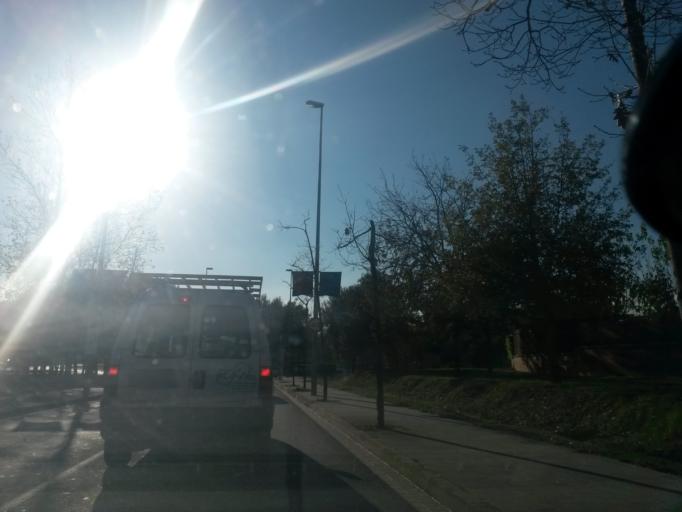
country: ES
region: Catalonia
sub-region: Provincia de Girona
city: Girona
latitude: 41.9931
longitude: 2.8125
